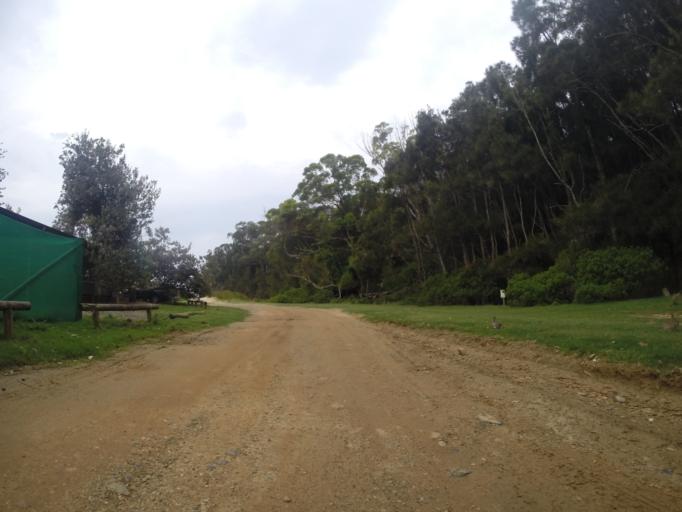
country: AU
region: New South Wales
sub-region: Eurobodalla
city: Batemans Bay
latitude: -35.6688
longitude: 150.3030
